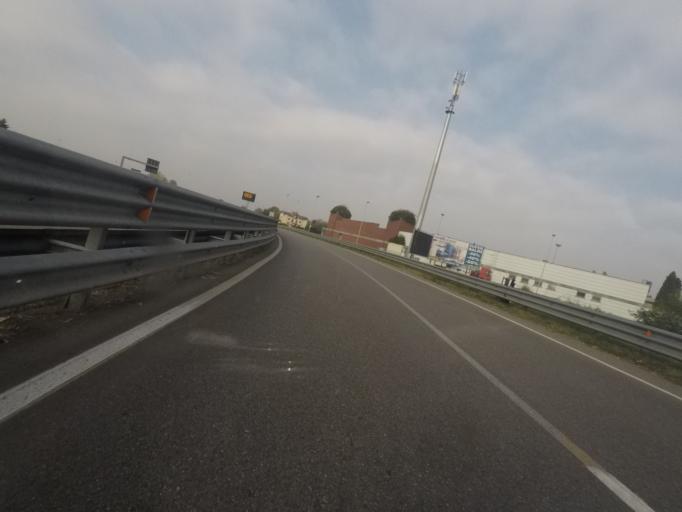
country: IT
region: Lombardy
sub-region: Provincia di Monza e Brianza
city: Vimercate
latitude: 45.6037
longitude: 9.3649
